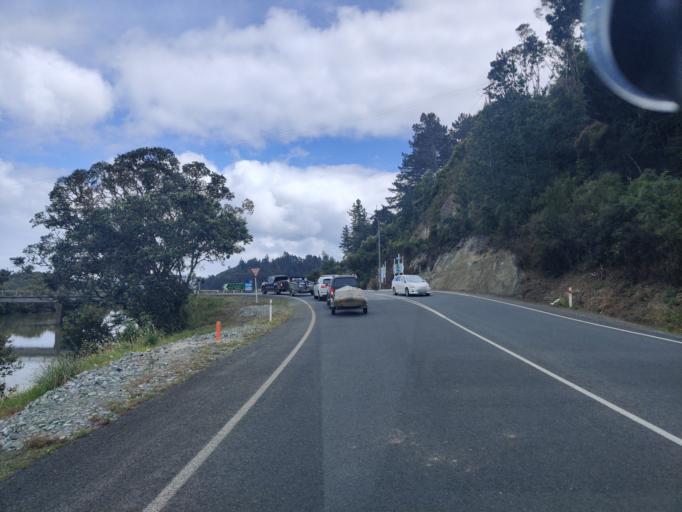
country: NZ
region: Northland
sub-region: Far North District
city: Kerikeri
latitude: -35.0822
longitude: 173.7619
